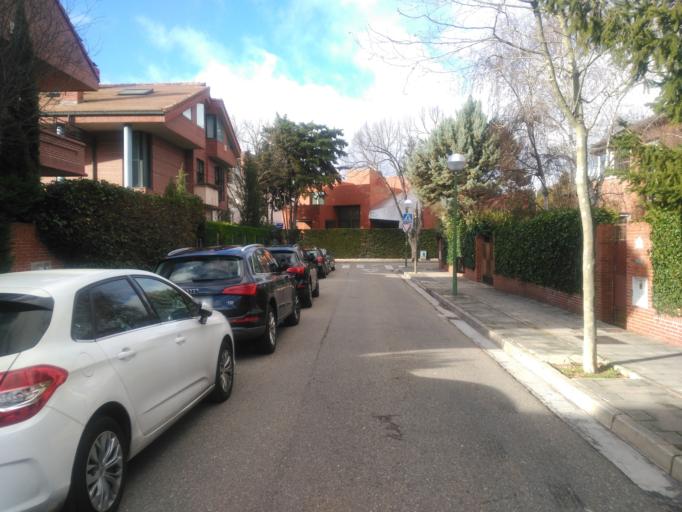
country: ES
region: Castille and Leon
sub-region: Provincia de Burgos
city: Burgos
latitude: 42.3364
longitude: -3.7124
